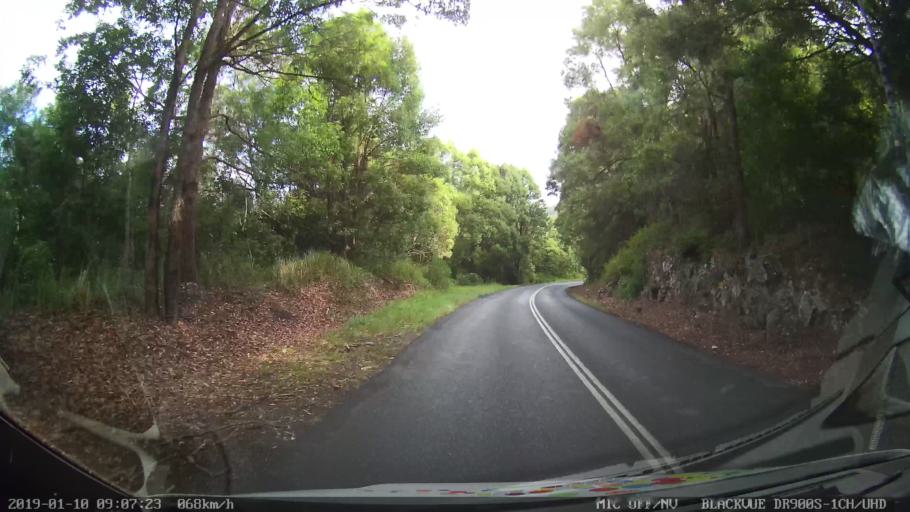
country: AU
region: New South Wales
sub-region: Coffs Harbour
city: Coffs Harbour
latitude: -30.2400
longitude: 153.0271
